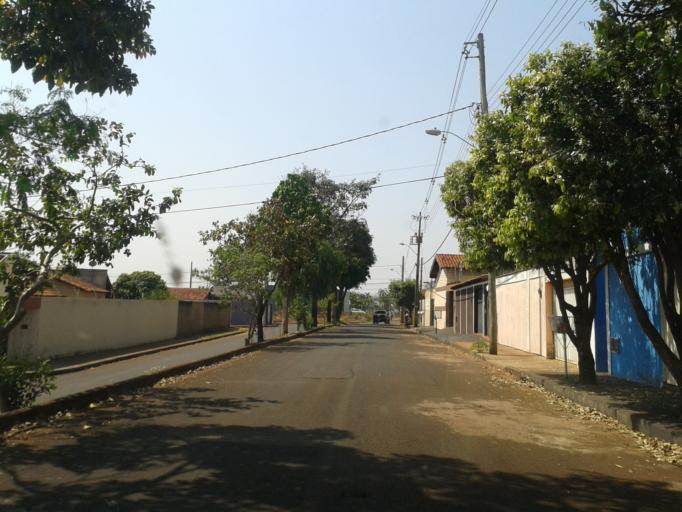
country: BR
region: Minas Gerais
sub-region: Ituiutaba
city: Ituiutaba
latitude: -18.9746
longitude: -49.4862
